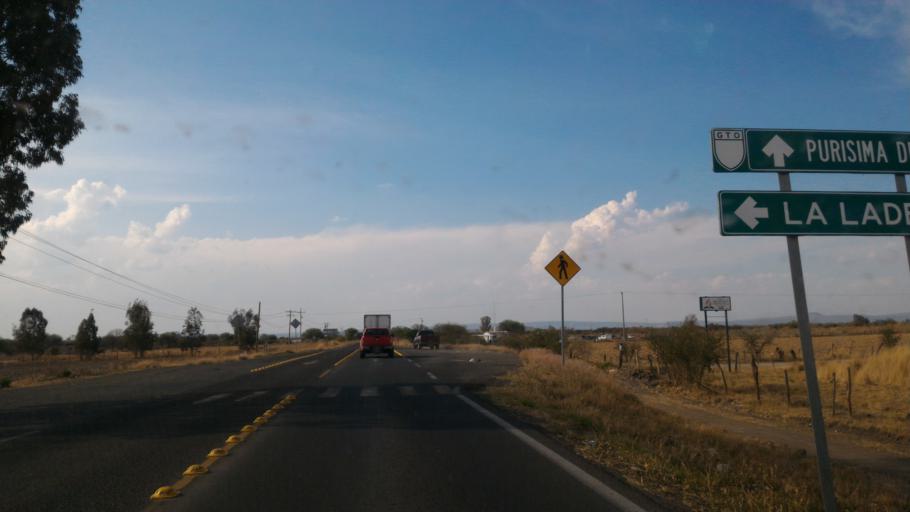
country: MX
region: Guanajuato
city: Ciudad Manuel Doblado
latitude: 20.7603
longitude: -101.9674
